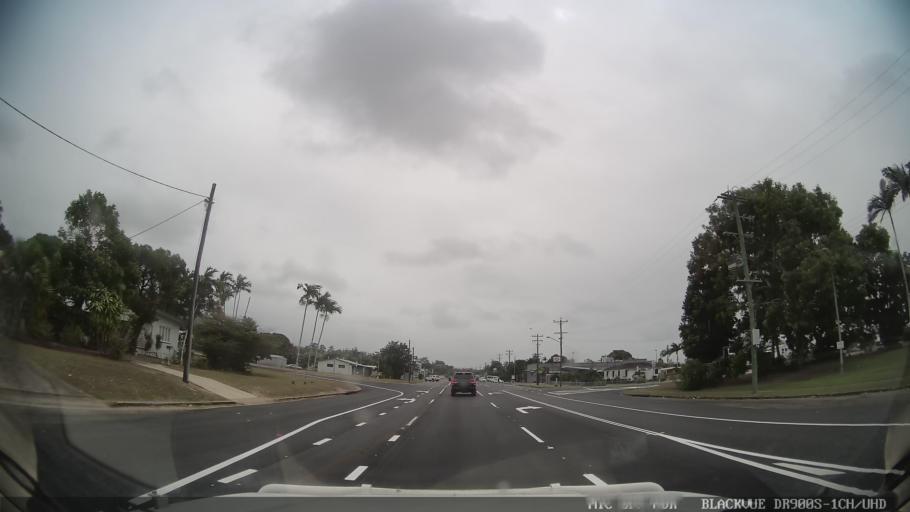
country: AU
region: Queensland
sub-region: Hinchinbrook
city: Ingham
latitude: -18.2587
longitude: 146.0199
